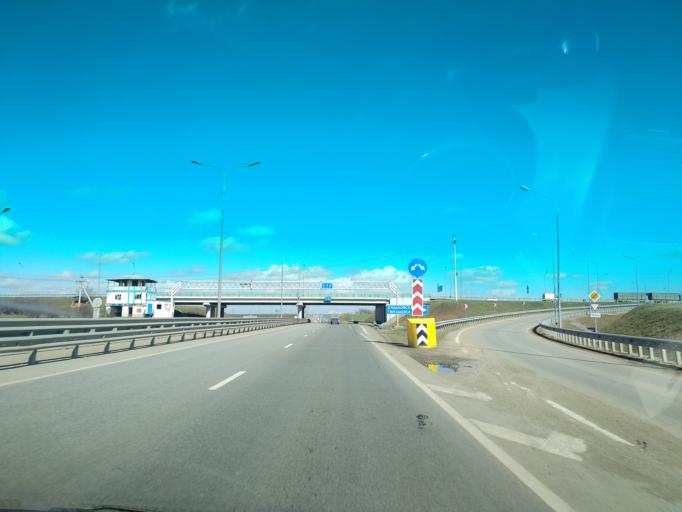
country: RU
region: Krasnodarskiy
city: Korenovsk
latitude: 45.4825
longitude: 39.4075
